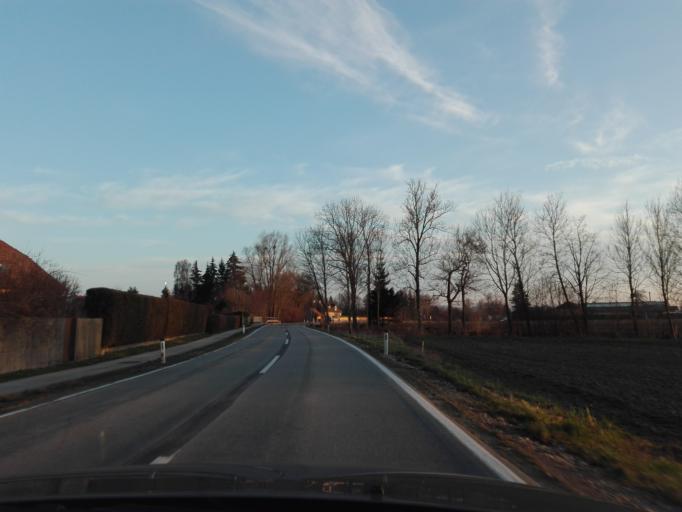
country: AT
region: Upper Austria
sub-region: Politischer Bezirk Urfahr-Umgebung
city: Feldkirchen an der Donau
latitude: 48.3248
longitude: 14.0119
